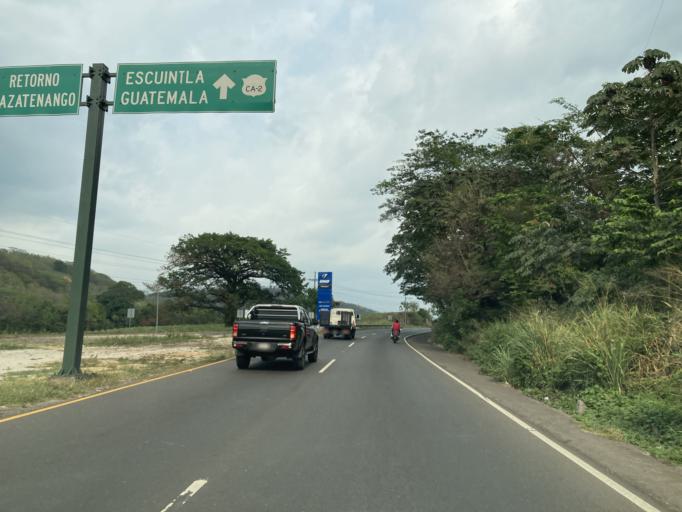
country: GT
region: Escuintla
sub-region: Municipio de La Democracia
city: La Democracia
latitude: 14.2667
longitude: -90.8872
